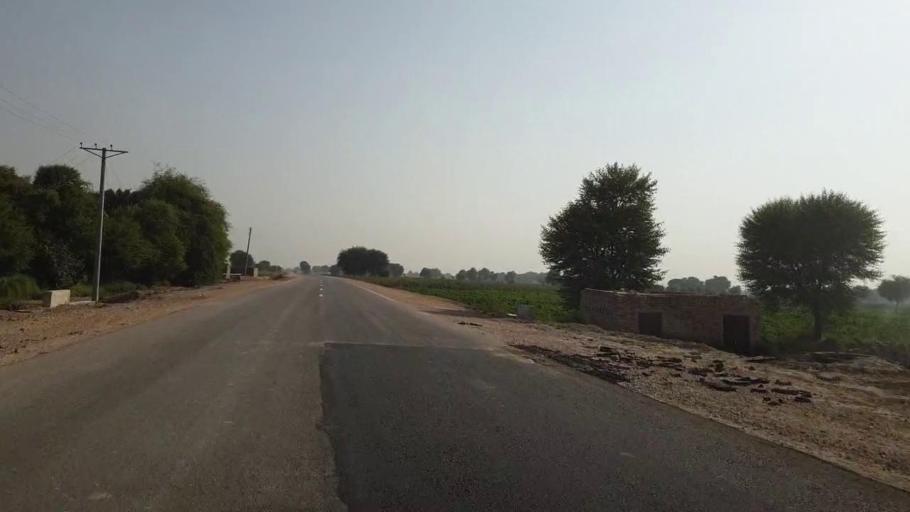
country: PK
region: Sindh
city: Bhan
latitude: 26.5322
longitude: 67.7887
